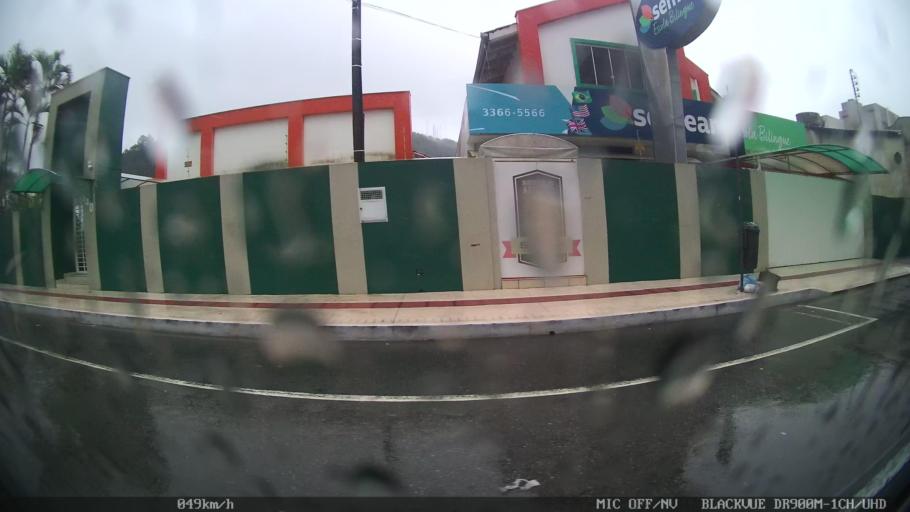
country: BR
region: Santa Catarina
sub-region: Balneario Camboriu
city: Balneario Camboriu
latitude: -26.9910
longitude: -48.6416
